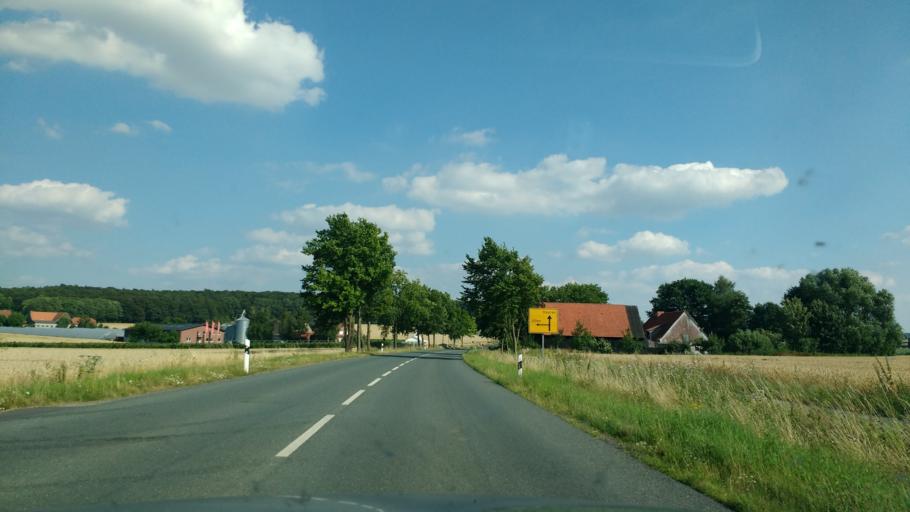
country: DE
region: North Rhine-Westphalia
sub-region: Regierungsbezirk Detmold
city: Salzkotten
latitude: 51.6640
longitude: 8.6424
